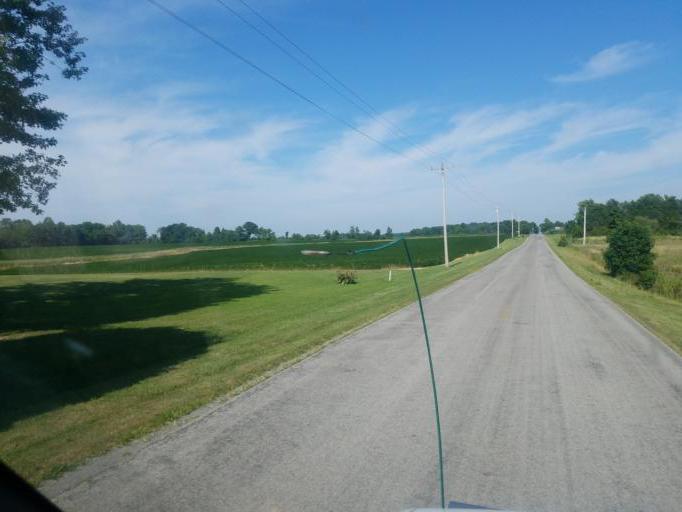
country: US
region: Ohio
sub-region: Logan County
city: Northwood
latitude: 40.5519
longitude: -83.6765
